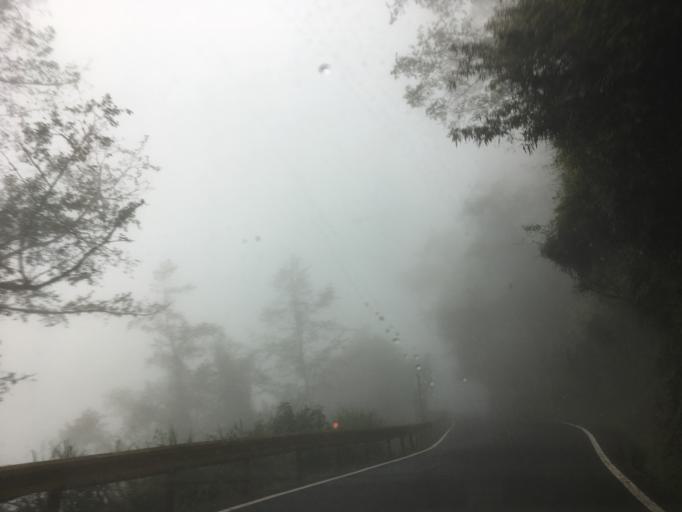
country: TW
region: Taiwan
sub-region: Hualien
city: Hualian
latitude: 24.1961
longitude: 121.4251
